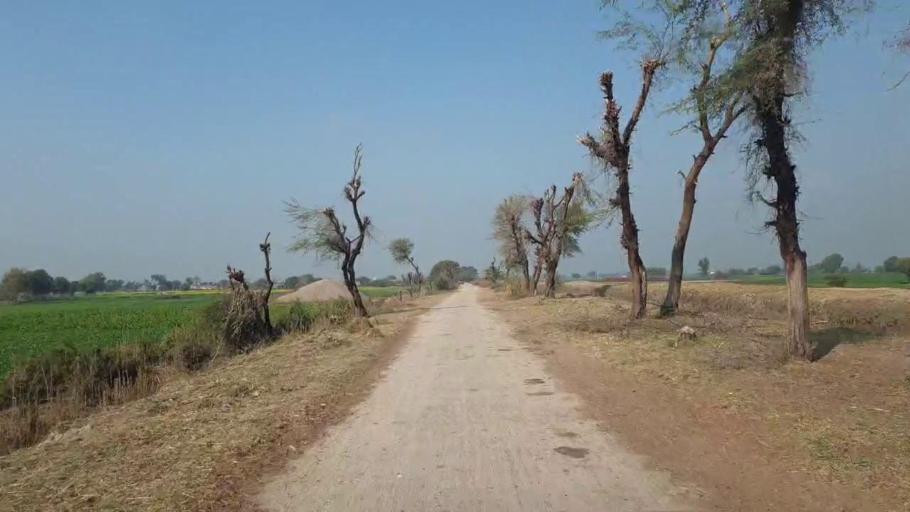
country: PK
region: Sindh
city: Shahdadpur
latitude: 26.0109
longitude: 68.5865
